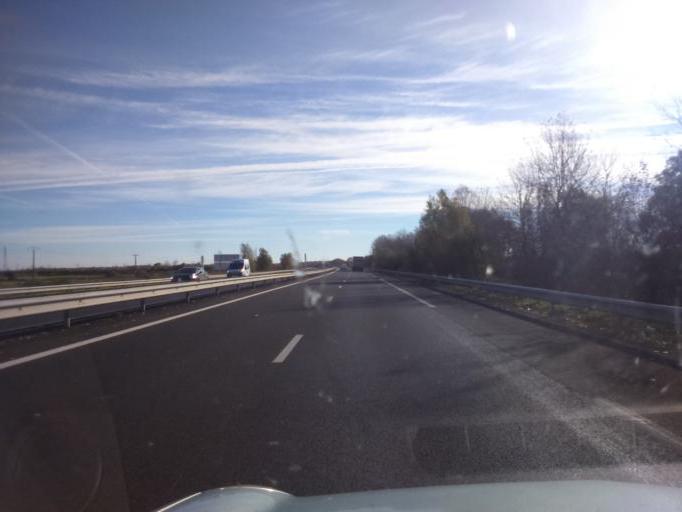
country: FR
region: Poitou-Charentes
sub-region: Departement de la Charente-Maritime
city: Breuil-Magne
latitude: 45.9588
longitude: -0.9433
